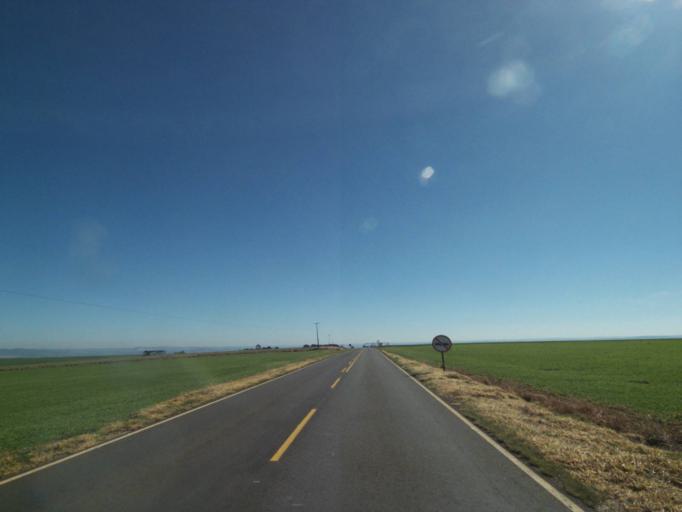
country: BR
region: Parana
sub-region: Tibagi
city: Tibagi
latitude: -24.5463
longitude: -50.2987
